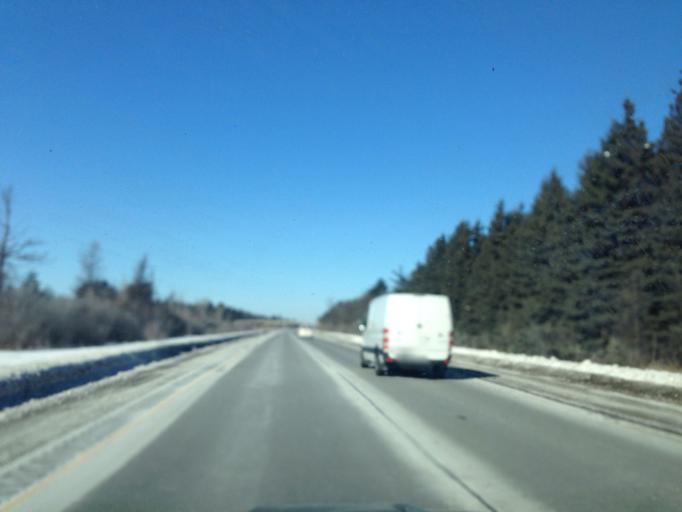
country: CA
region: Ontario
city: Ottawa
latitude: 45.3655
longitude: -75.5127
